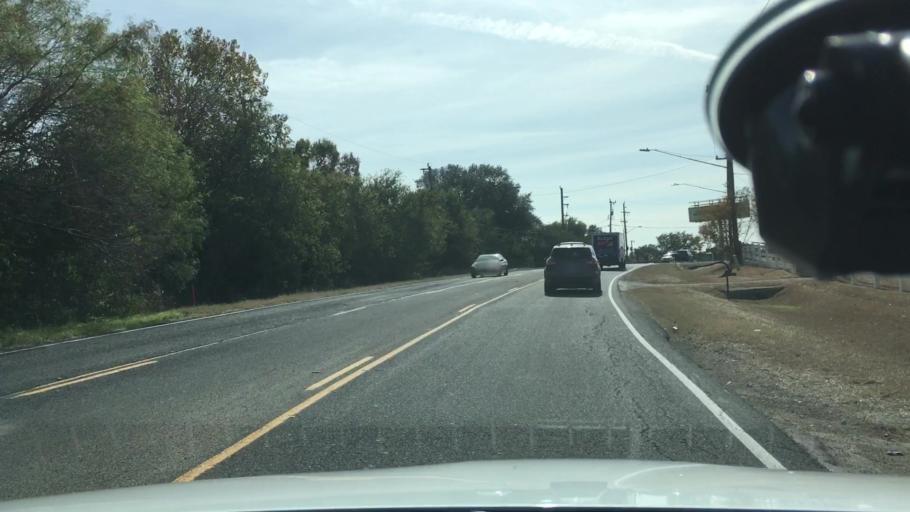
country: US
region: Texas
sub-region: Bexar County
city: Windcrest
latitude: 29.5739
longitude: -98.4182
